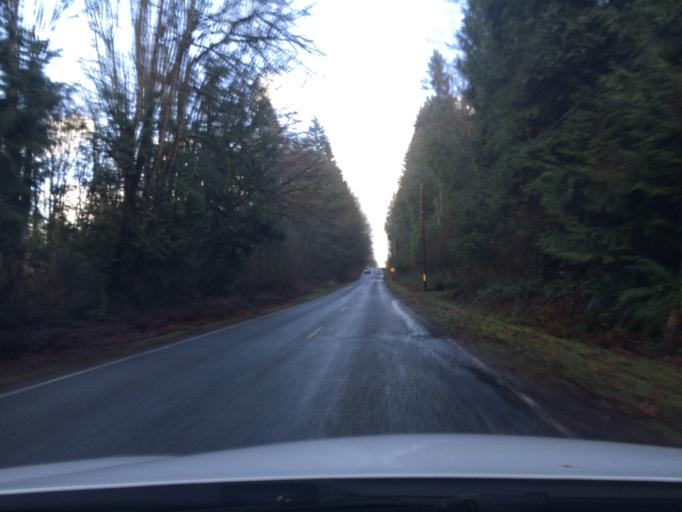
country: US
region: Washington
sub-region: Whatcom County
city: Blaine
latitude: 48.9939
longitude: -122.6856
